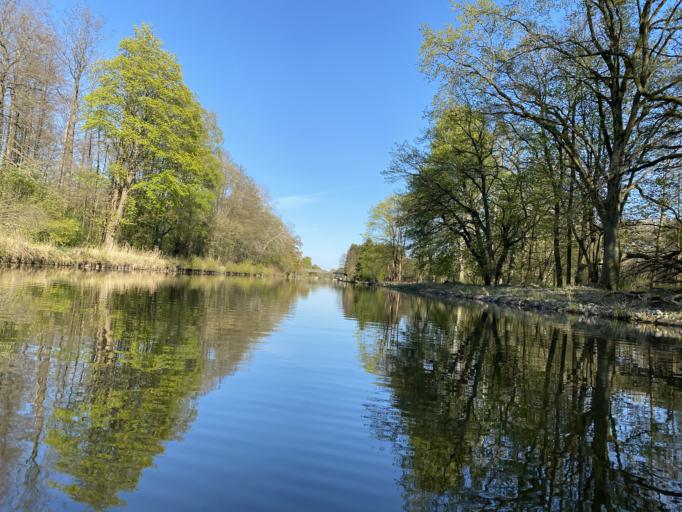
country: DE
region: Brandenburg
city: Mullrose
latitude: 52.2471
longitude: 14.4488
